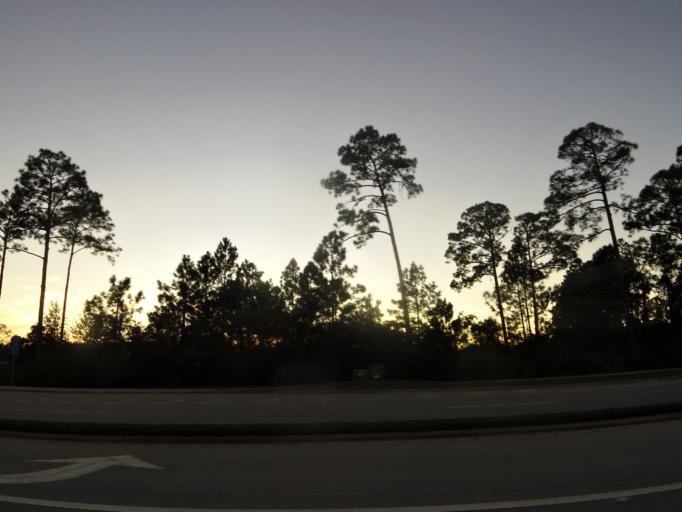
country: US
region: Florida
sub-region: Flagler County
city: Palm Coast
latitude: 29.5764
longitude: -81.2548
